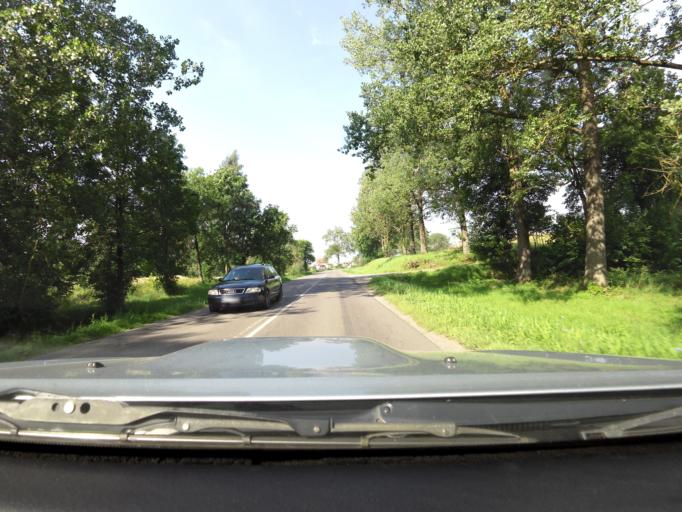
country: PL
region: Warmian-Masurian Voivodeship
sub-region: Powiat olecki
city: Olecko
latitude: 54.0414
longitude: 22.4807
